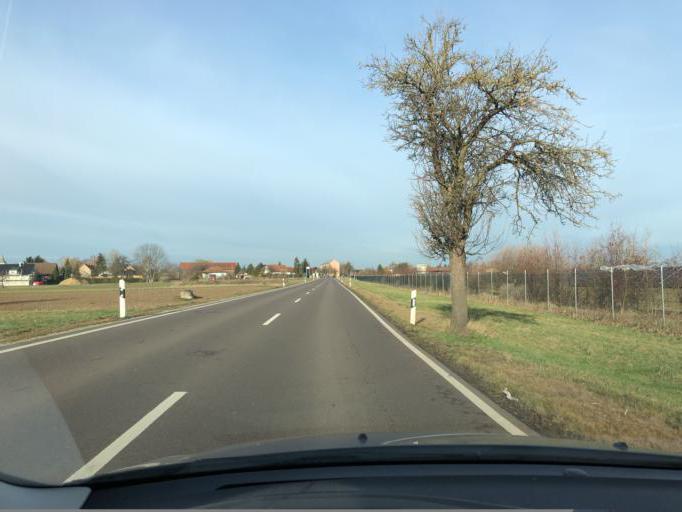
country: DE
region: Saxony-Anhalt
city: Reichardtswerben
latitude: 51.2490
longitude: 11.9668
